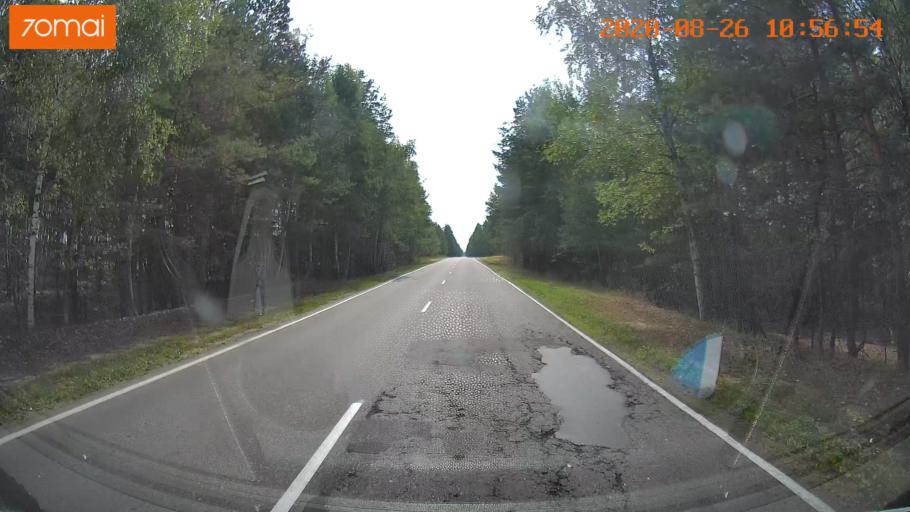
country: RU
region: Rjazan
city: Izhevskoye
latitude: 54.5972
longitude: 41.1926
